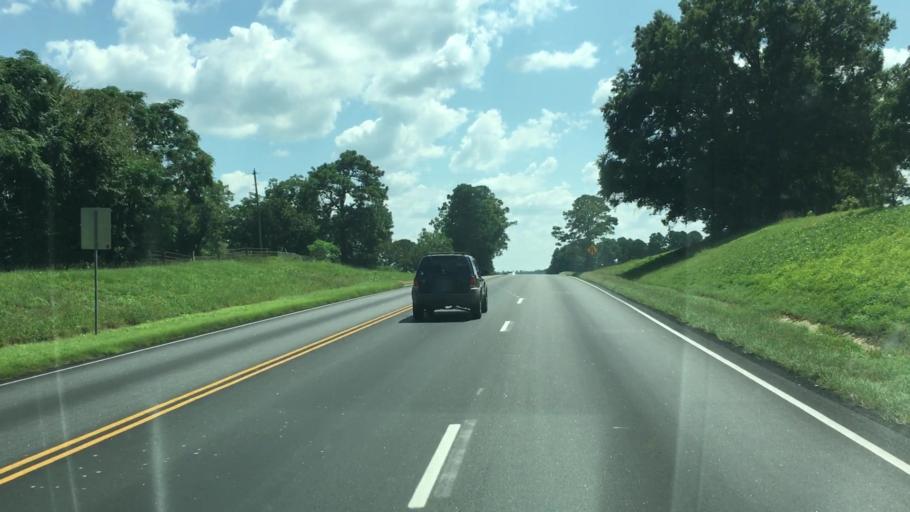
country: US
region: Georgia
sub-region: Morgan County
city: Madison
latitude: 33.6586
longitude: -83.4460
